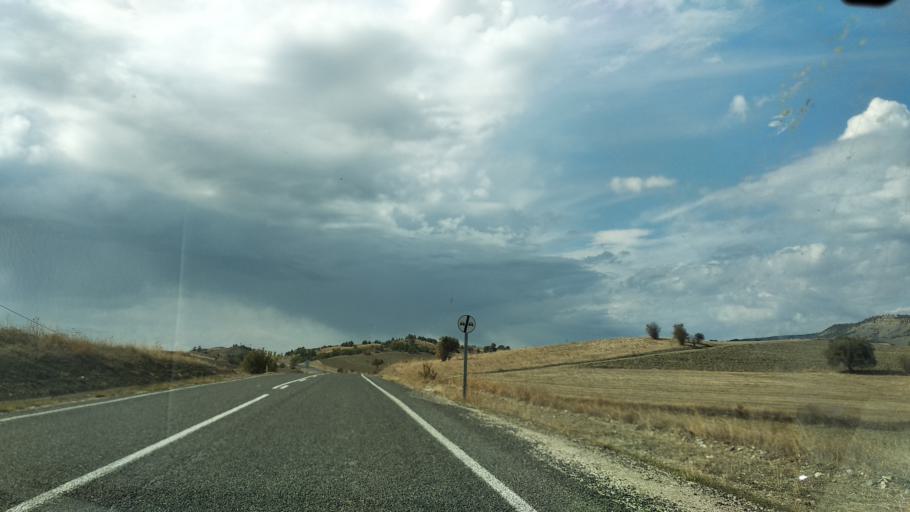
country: TR
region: Bolu
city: Seben
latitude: 40.3885
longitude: 31.5415
